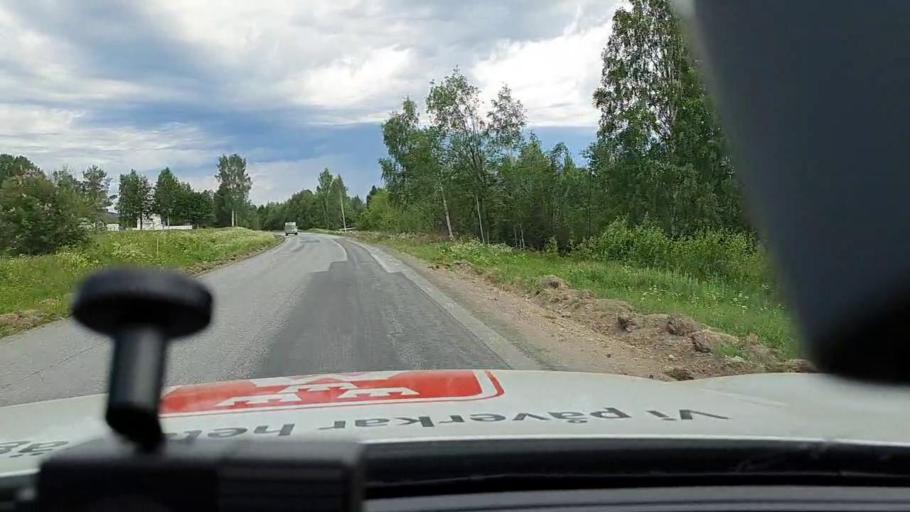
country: SE
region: Norrbotten
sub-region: Bodens Kommun
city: Saevast
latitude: 65.7672
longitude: 21.6905
